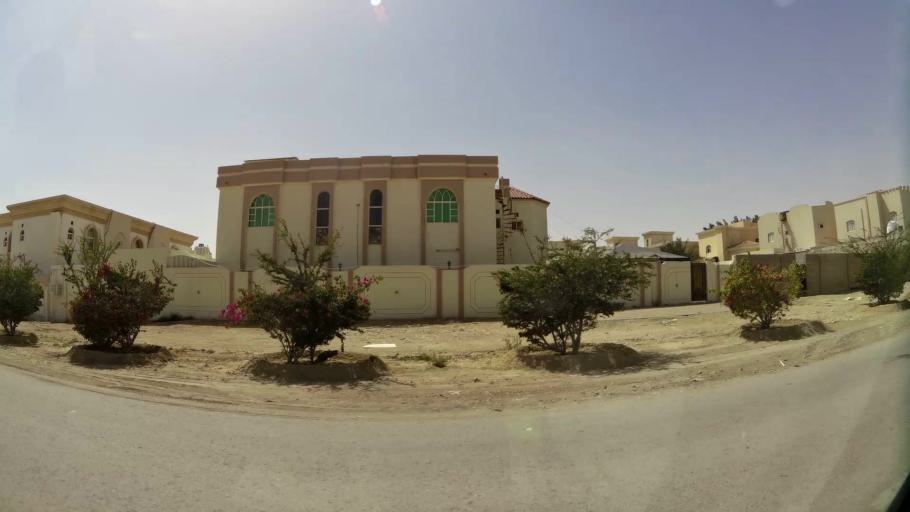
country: QA
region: Baladiyat Umm Salal
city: Umm Salal Muhammad
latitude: 25.3790
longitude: 51.4196
